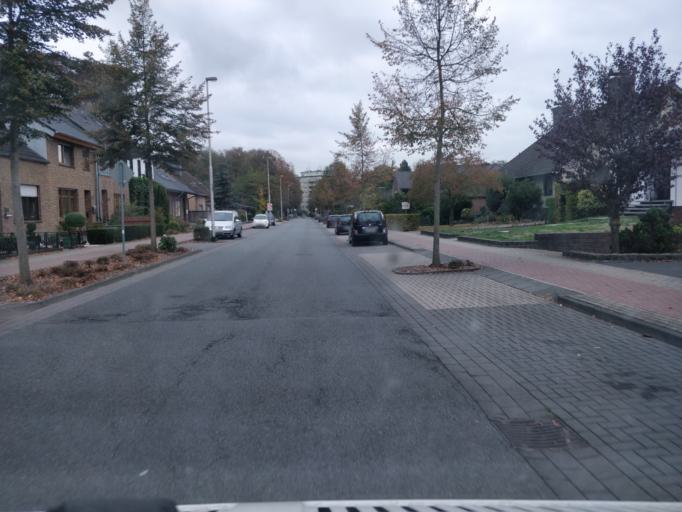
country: DE
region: North Rhine-Westphalia
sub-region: Regierungsbezirk Dusseldorf
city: Emmerich
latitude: 51.8462
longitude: 6.2421
